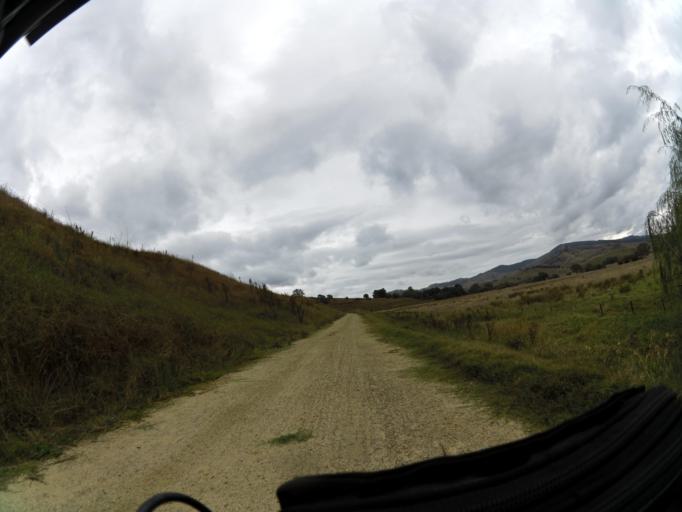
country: AU
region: New South Wales
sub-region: Albury Municipality
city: East Albury
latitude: -36.1924
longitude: 147.2965
